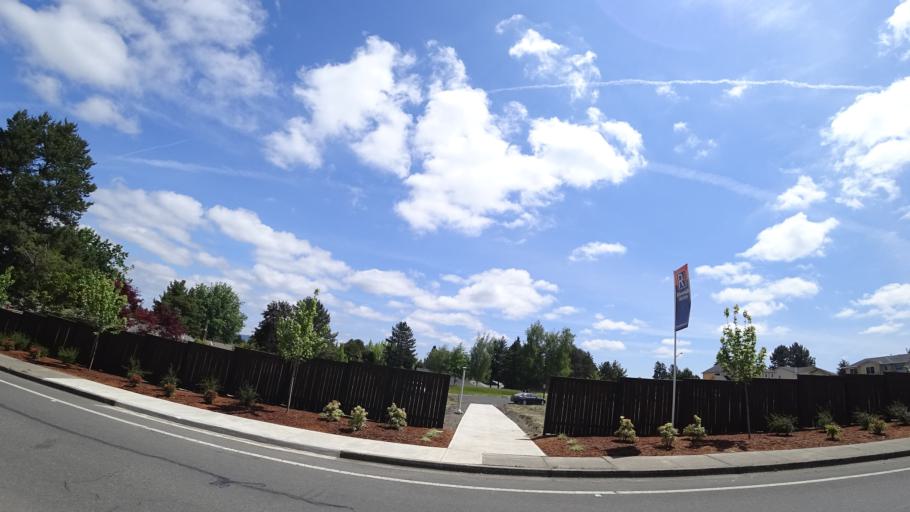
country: US
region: Oregon
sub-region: Washington County
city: King City
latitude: 45.4333
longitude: -122.8157
